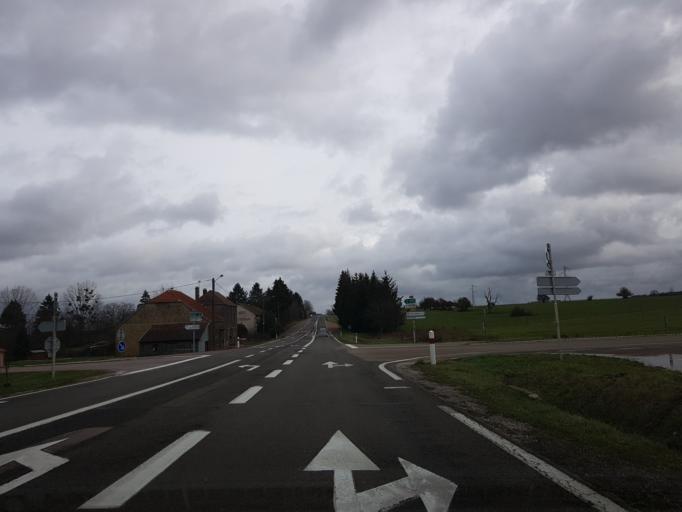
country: FR
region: Champagne-Ardenne
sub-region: Departement de la Haute-Marne
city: Chalindrey
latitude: 47.8176
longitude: 5.4906
